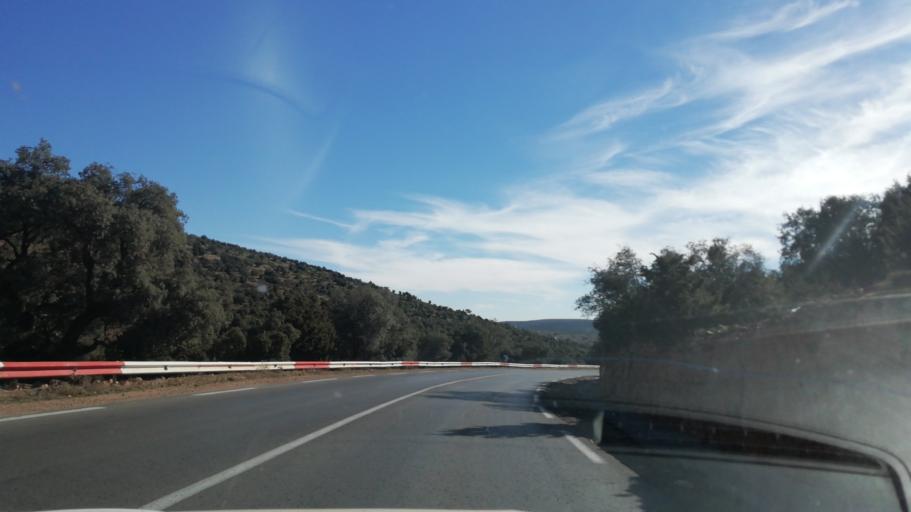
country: DZ
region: Tlemcen
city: Sebdou
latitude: 34.7385
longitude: -1.3381
